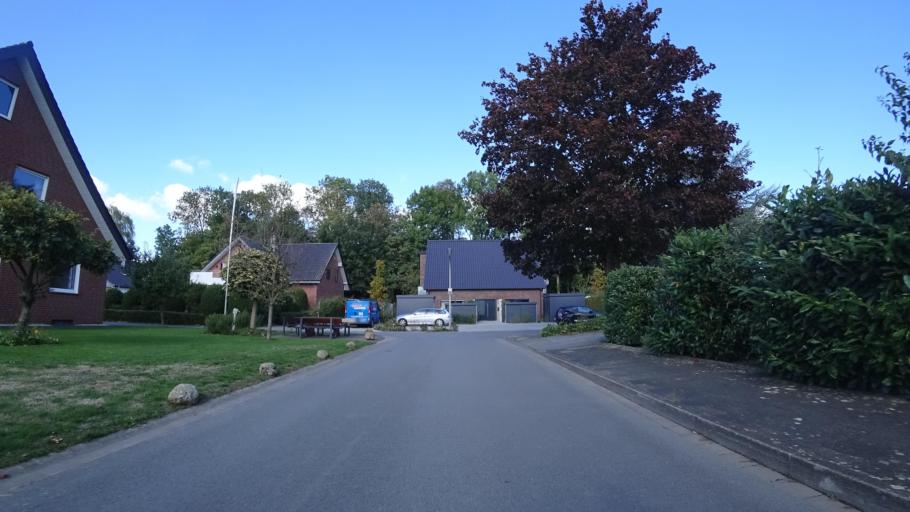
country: DE
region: North Rhine-Westphalia
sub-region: Regierungsbezirk Detmold
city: Rheda-Wiedenbruck
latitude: 51.8615
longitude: 8.2976
